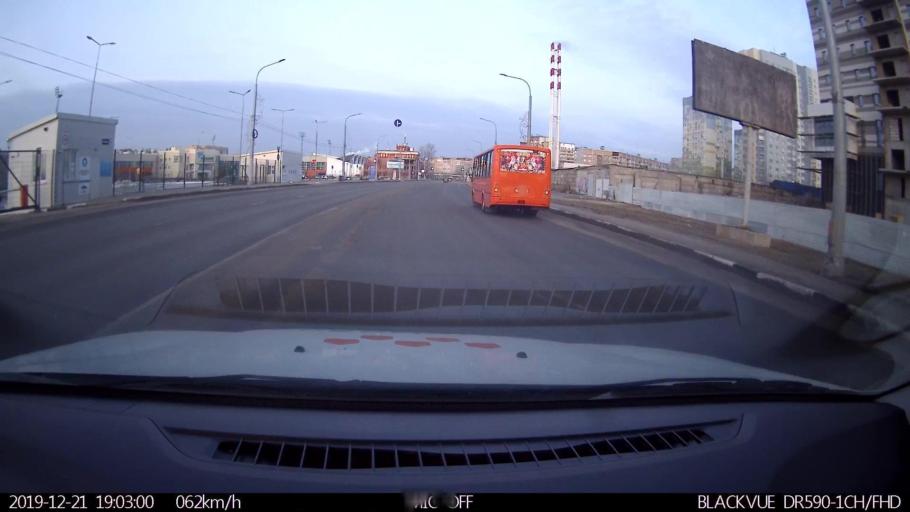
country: RU
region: Nizjnij Novgorod
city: Nizhniy Novgorod
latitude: 56.3386
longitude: 43.9468
